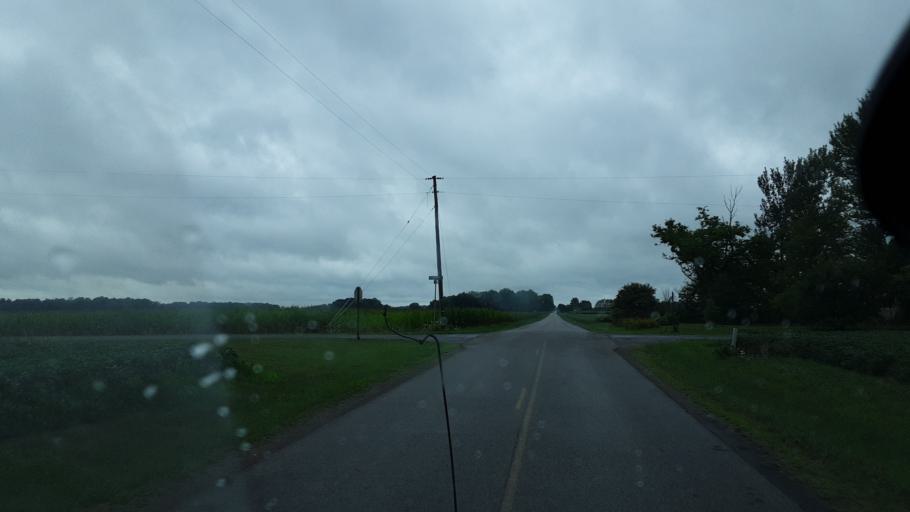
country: US
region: Ohio
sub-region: Van Wert County
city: Van Wert
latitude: 40.8004
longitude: -84.6657
